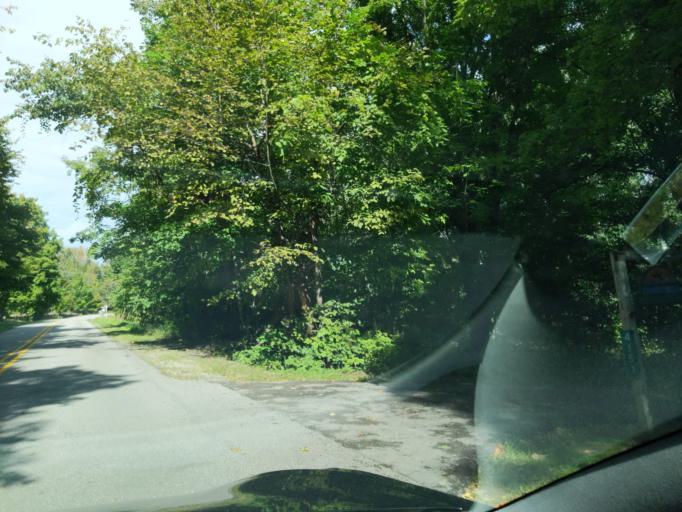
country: US
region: Michigan
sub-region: Antrim County
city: Bellaire
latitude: 44.9731
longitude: -85.3238
